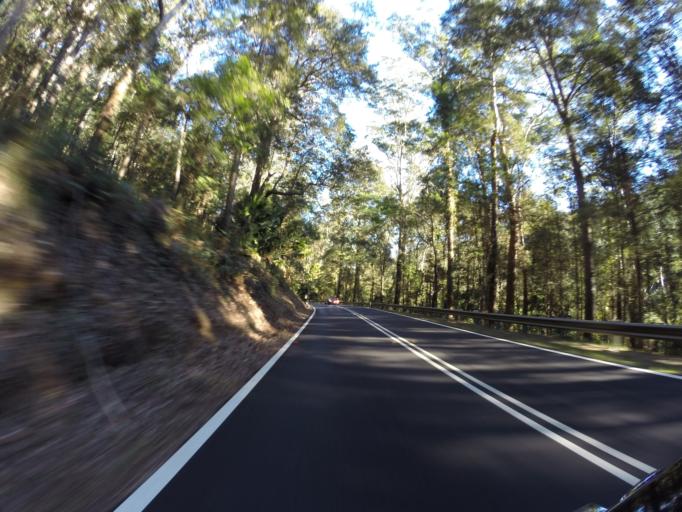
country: AU
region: New South Wales
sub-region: Wollongong
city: Helensburgh
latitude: -34.1595
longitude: 151.0170
